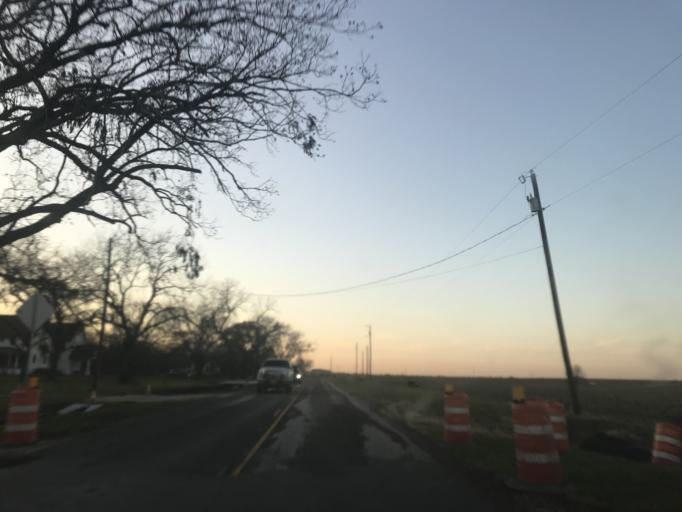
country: US
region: Texas
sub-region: Williamson County
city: Hutto
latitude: 30.4981
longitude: -97.5042
